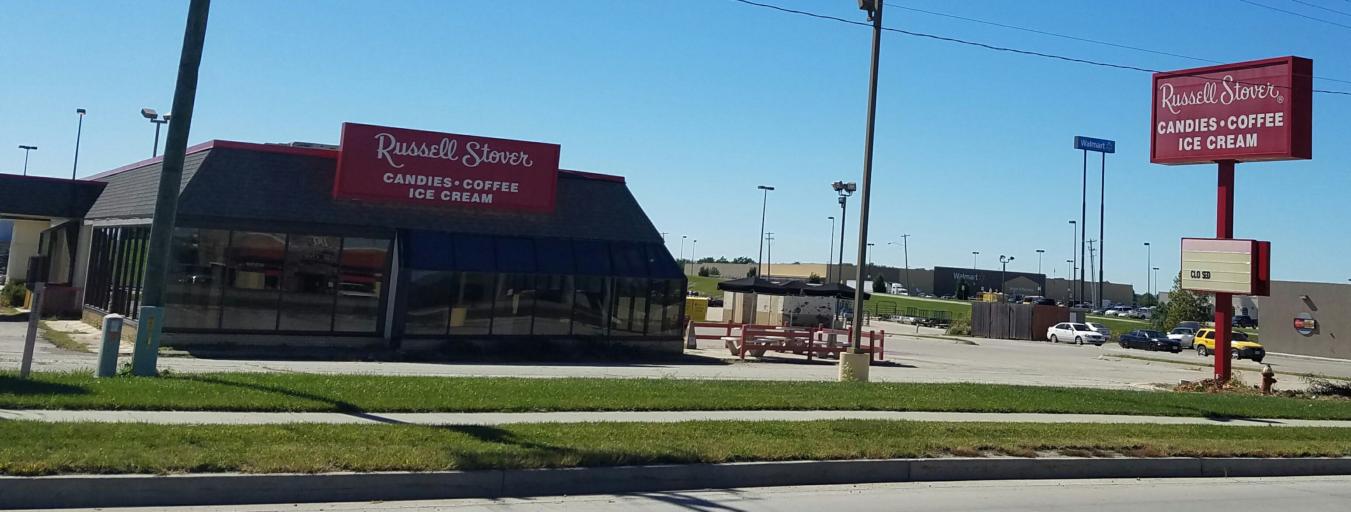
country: US
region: Missouri
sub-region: Harrison County
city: Bethany
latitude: 40.2663
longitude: -94.0142
